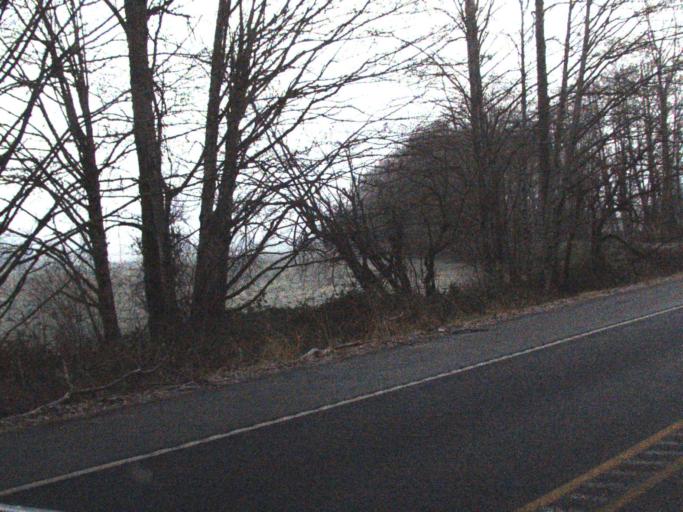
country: US
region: Washington
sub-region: Skagit County
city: Sedro-Woolley
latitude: 48.5246
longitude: -121.9661
